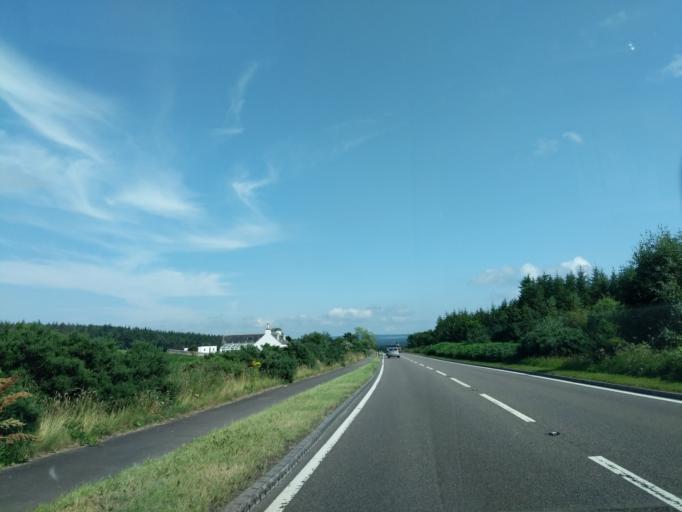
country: GB
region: Scotland
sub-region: Moray
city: Lhanbryd
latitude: 57.6276
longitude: -3.1655
